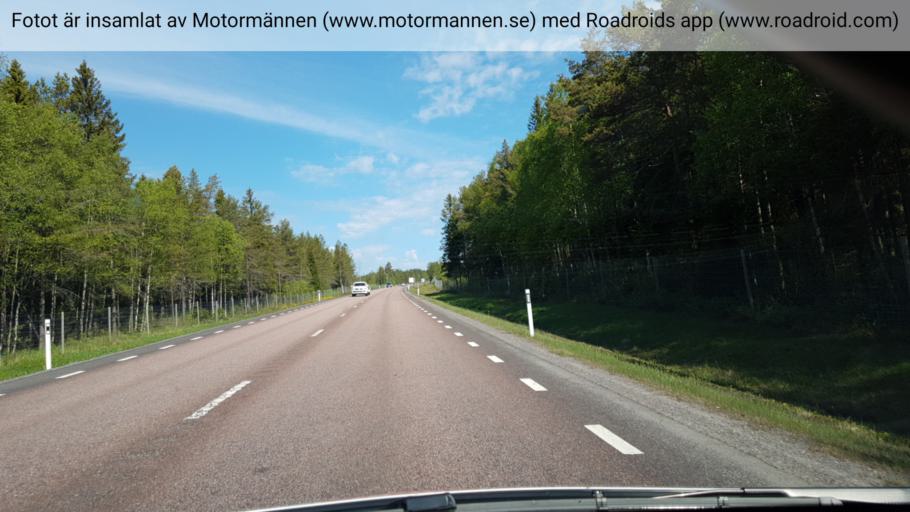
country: SE
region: Vaesterbotten
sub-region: Skelleftea Kommun
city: Burea
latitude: 64.4146
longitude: 21.2914
